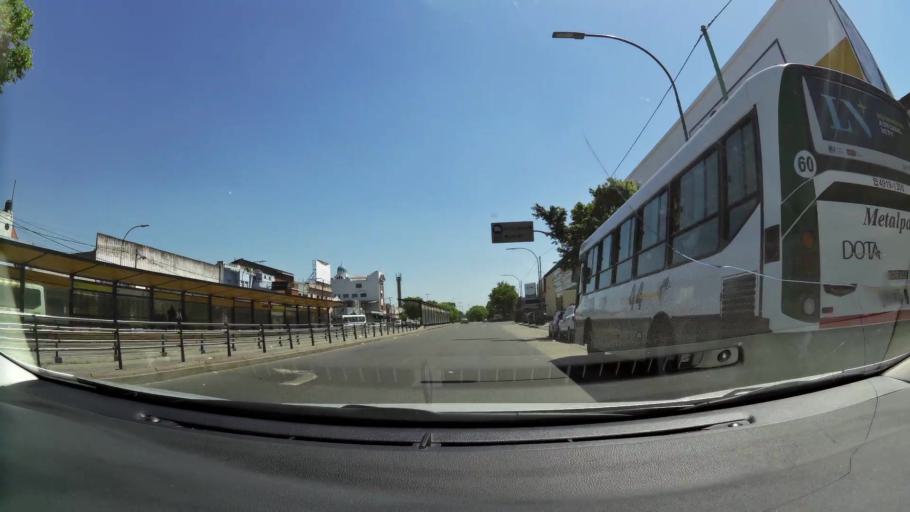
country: AR
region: Buenos Aires
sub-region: Partido de Avellaneda
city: Avellaneda
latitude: -34.6548
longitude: -58.4170
